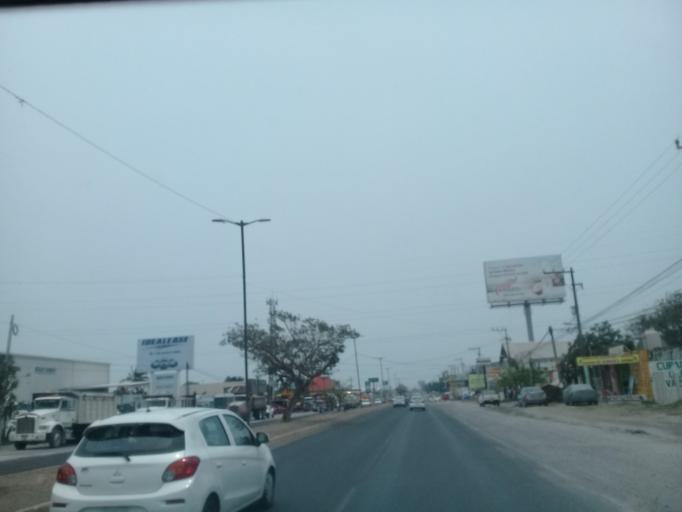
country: MX
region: Veracruz
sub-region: Veracruz
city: Las Amapolas
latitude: 19.1615
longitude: -96.2054
